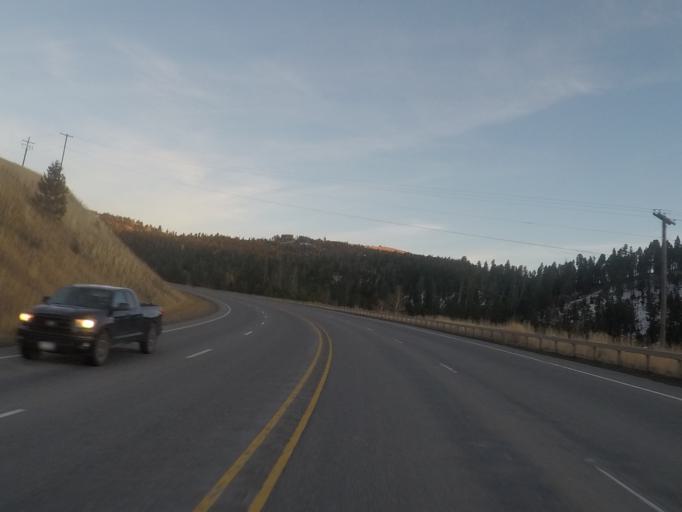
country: US
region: Montana
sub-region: Lewis and Clark County
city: Helena West Side
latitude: 46.5594
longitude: -112.3710
